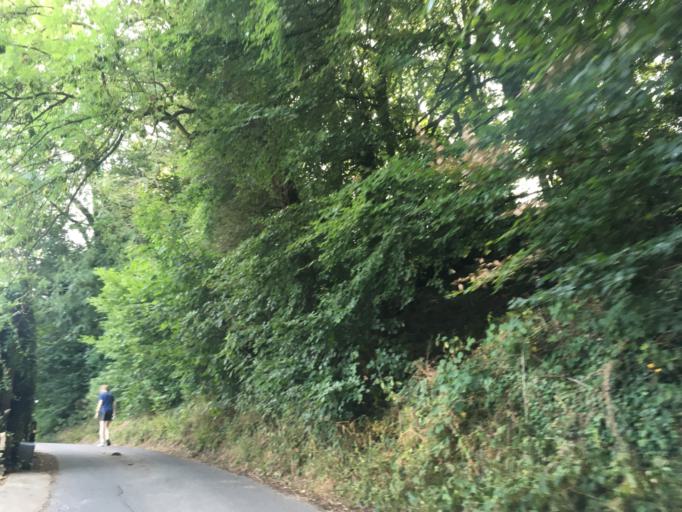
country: GB
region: England
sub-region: Gloucestershire
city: Nailsworth
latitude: 51.6754
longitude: -2.2316
